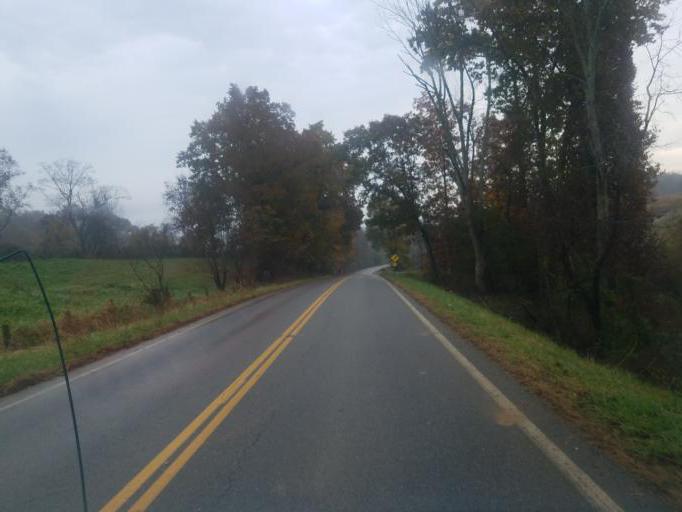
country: US
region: Ohio
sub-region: Morgan County
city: McConnelsville
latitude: 39.4732
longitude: -81.8832
